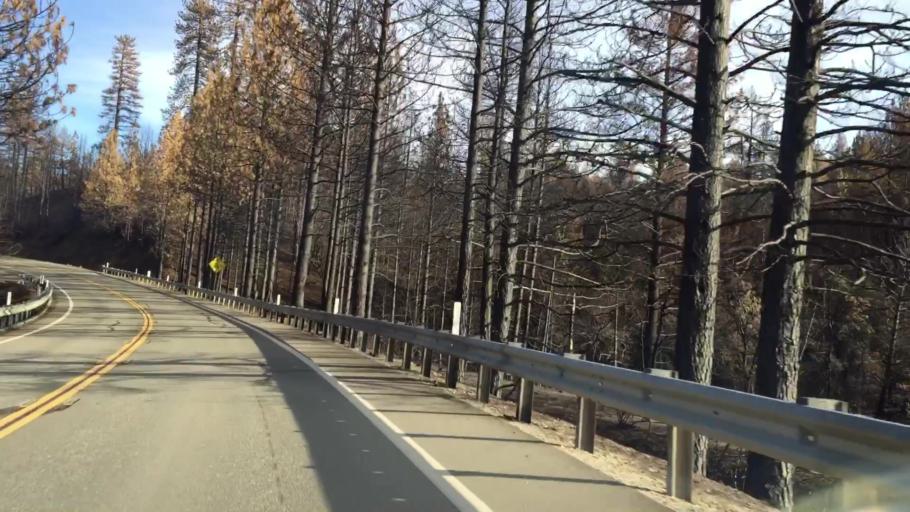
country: US
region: California
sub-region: Butte County
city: Magalia
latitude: 39.7282
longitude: -121.4948
